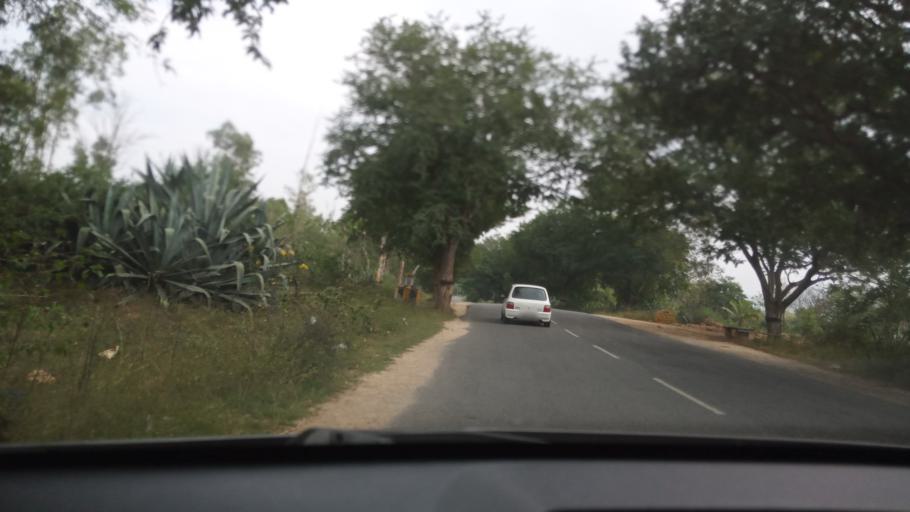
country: IN
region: Andhra Pradesh
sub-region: Chittoor
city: Pakala
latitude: 13.6563
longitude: 78.8463
